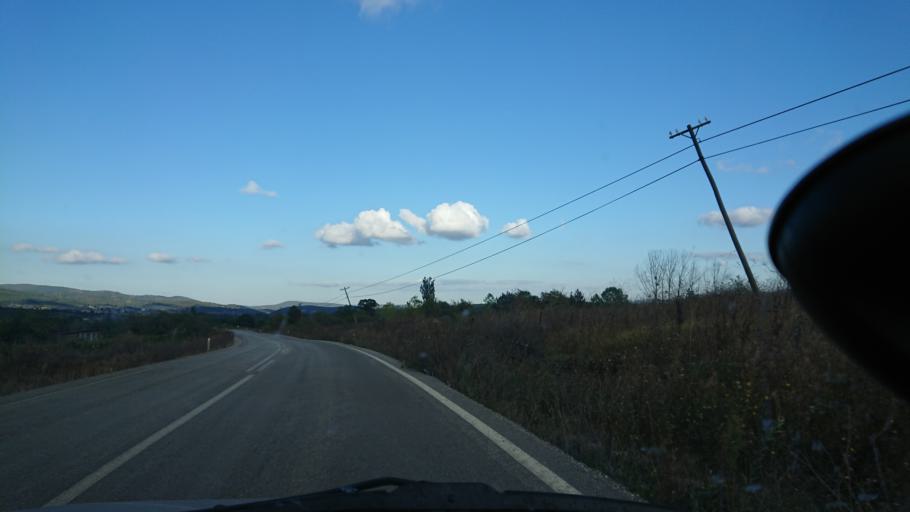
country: TR
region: Bilecik
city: Pazaryeri
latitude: 40.0099
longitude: 29.8090
